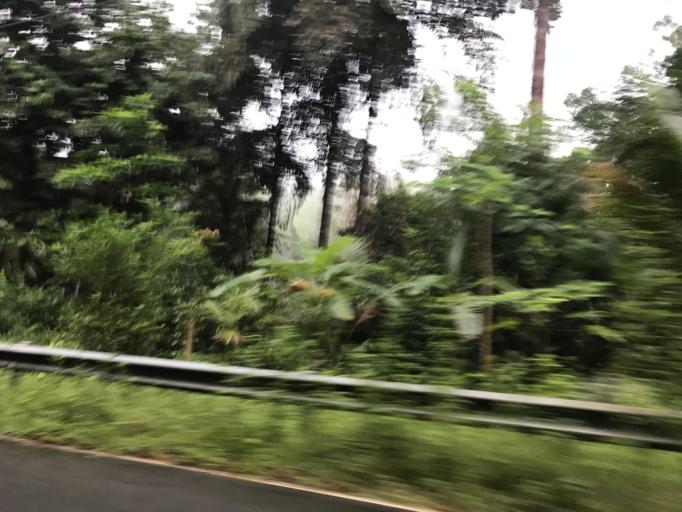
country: LK
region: Western
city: Horawala Junction
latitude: 6.5438
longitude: 80.2814
